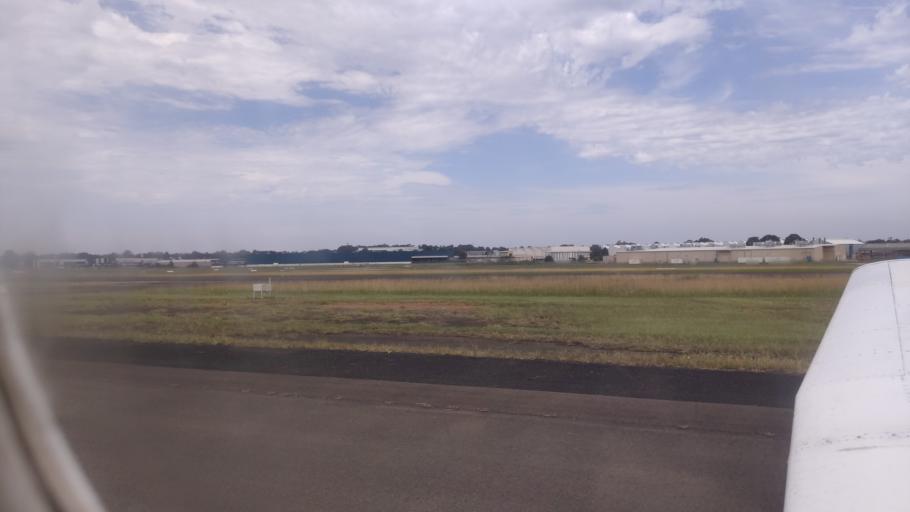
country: AU
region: New South Wales
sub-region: Bankstown
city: Milperra
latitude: -33.9243
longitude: 150.9948
